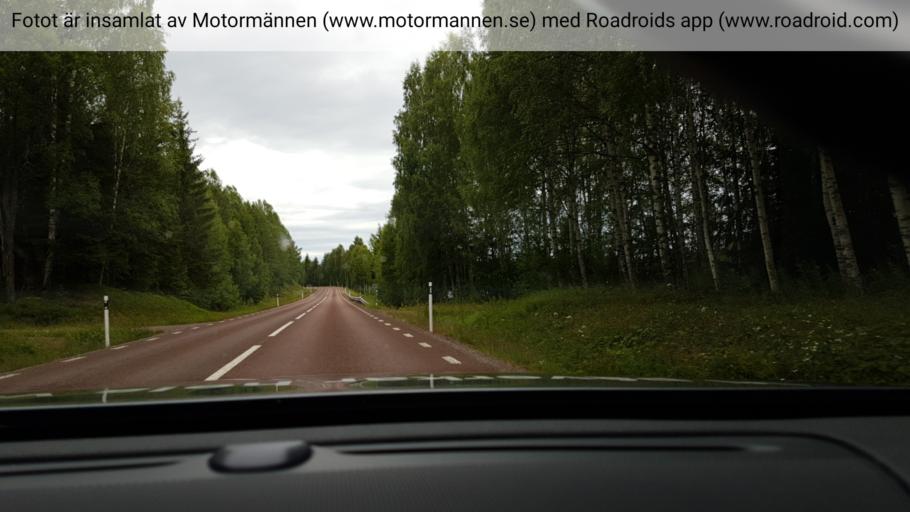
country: SE
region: Dalarna
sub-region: Gagnefs Kommun
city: Mockfjard
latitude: 60.5080
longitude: 14.8733
